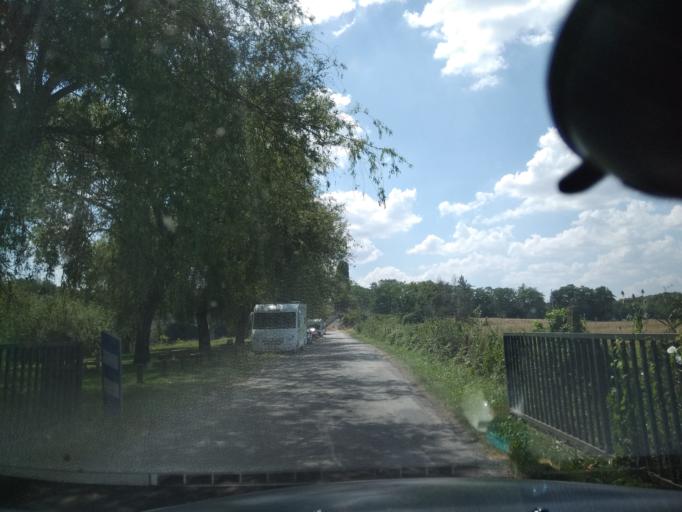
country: FR
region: Centre
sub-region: Departement d'Indre-et-Loire
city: Civray-de-Touraine
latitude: 47.3284
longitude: 1.0849
